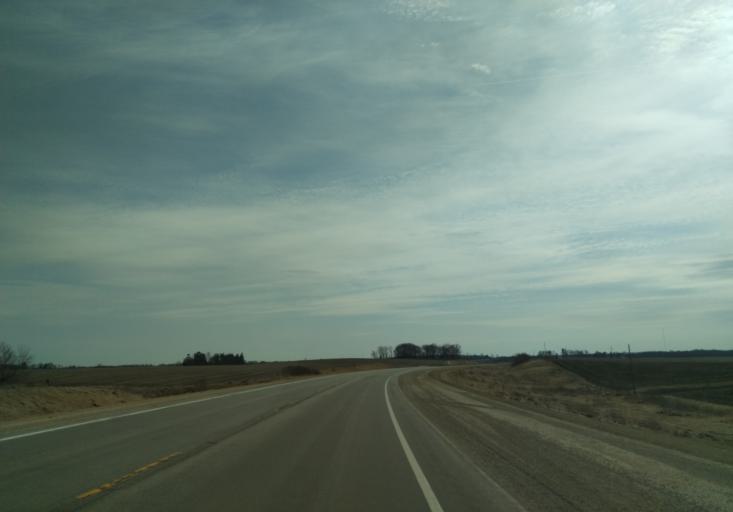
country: US
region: Iowa
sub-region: Winneshiek County
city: Decorah
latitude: 43.3647
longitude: -91.8047
